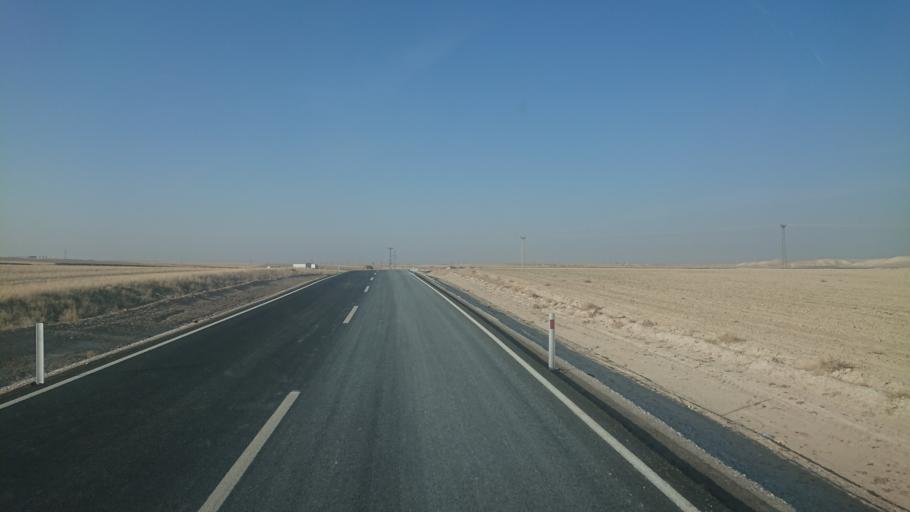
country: TR
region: Aksaray
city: Sultanhani
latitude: 38.0877
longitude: 33.6130
